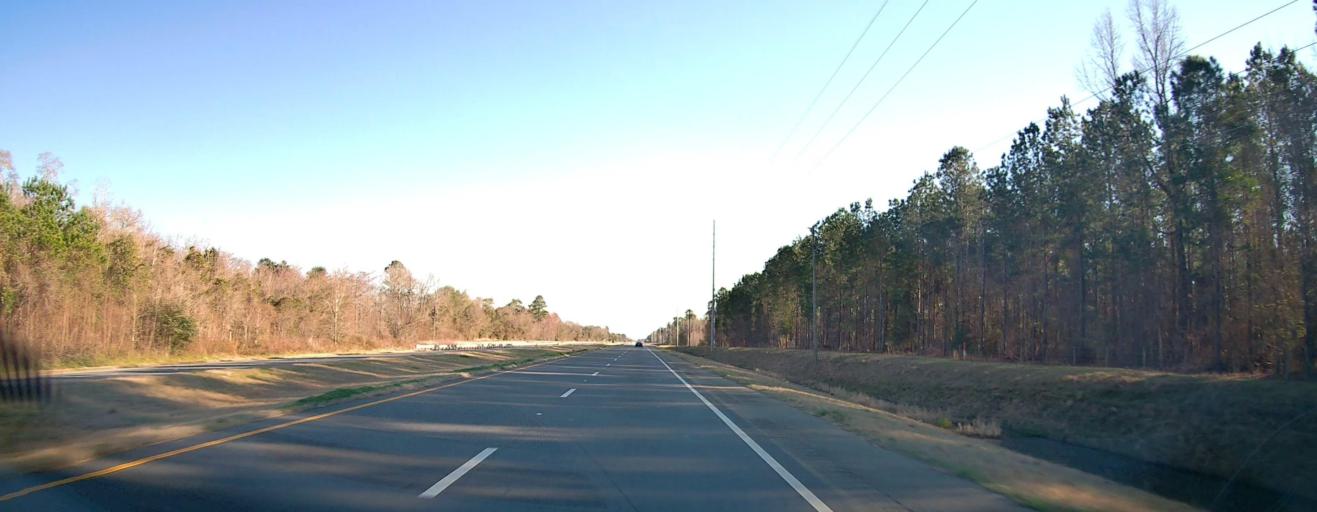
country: US
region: Georgia
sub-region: Lee County
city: Leesburg
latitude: 31.8539
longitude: -84.2300
